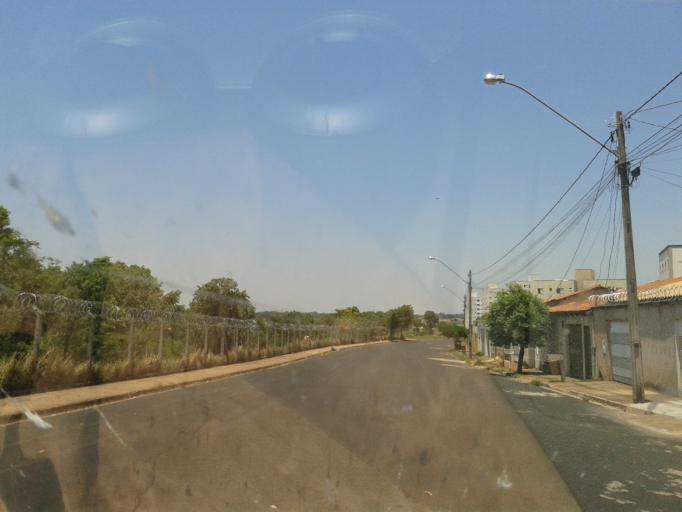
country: BR
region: Minas Gerais
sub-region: Uberlandia
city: Uberlandia
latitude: -18.9640
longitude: -48.3114
